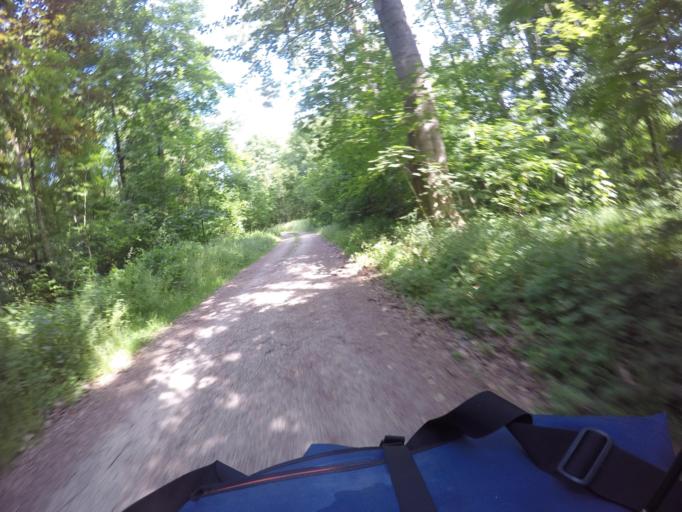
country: DE
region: Baden-Wuerttemberg
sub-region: Karlsruhe Region
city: Otigheim
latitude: 48.9051
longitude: 8.2343
